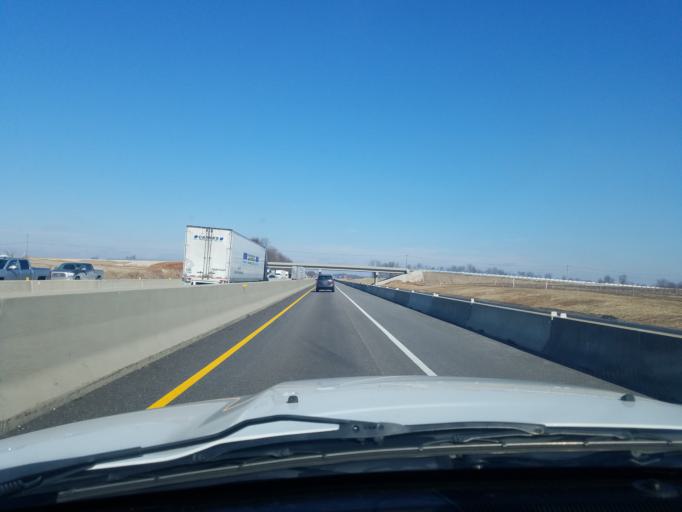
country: US
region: Kentucky
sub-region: Hardin County
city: Elizabethtown
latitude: 37.5713
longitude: -85.8741
